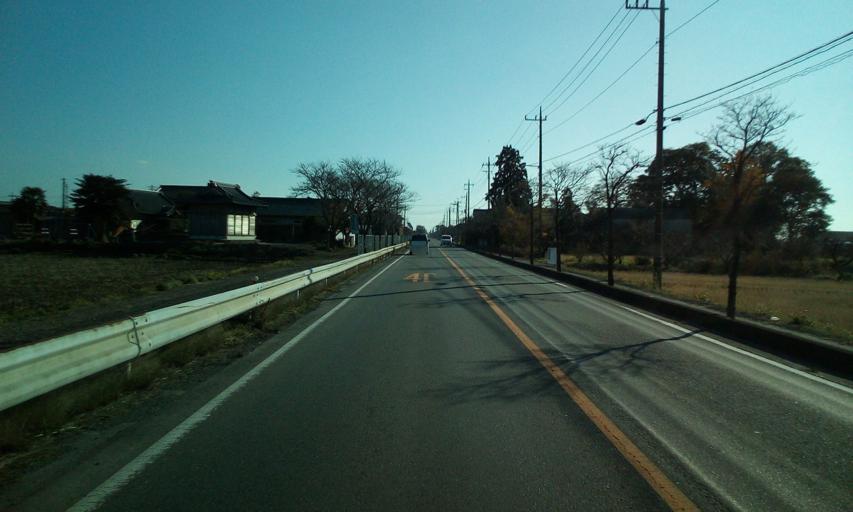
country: JP
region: Saitama
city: Sugito
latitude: 36.0300
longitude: 139.7877
